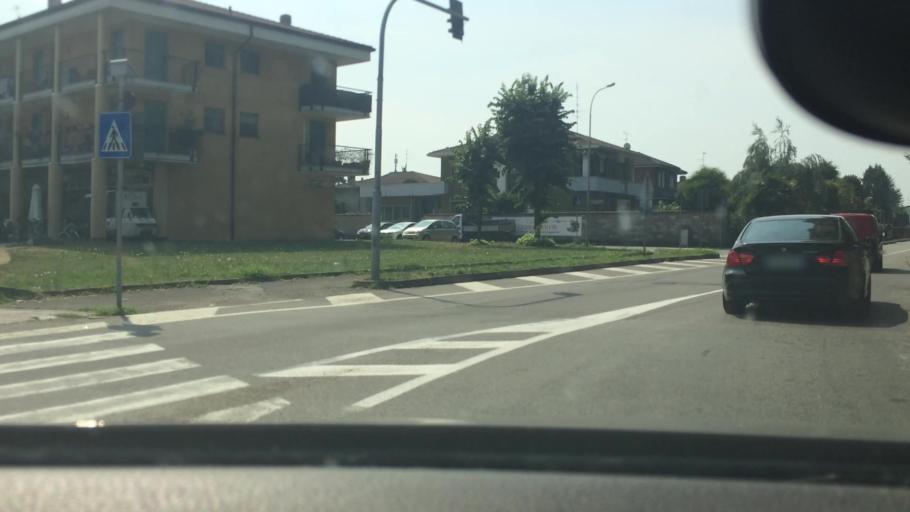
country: IT
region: Lombardy
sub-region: Citta metropolitana di Milano
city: Casorezzo
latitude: 45.5237
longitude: 8.9057
